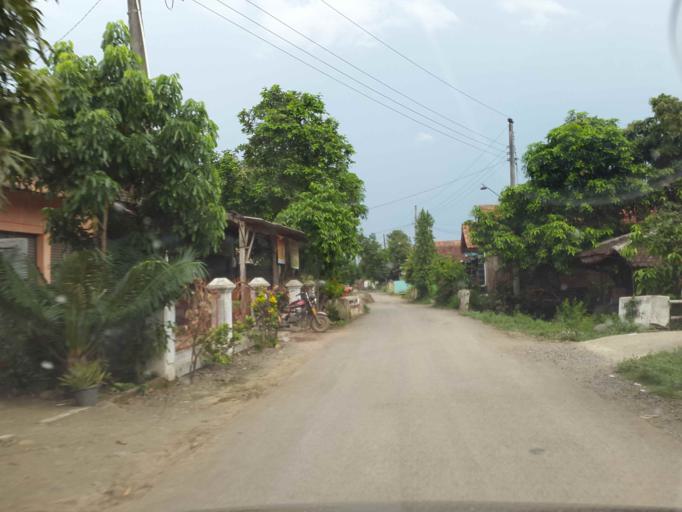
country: ID
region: Central Java
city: Ketanggungan
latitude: -6.9819
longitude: 108.9568
